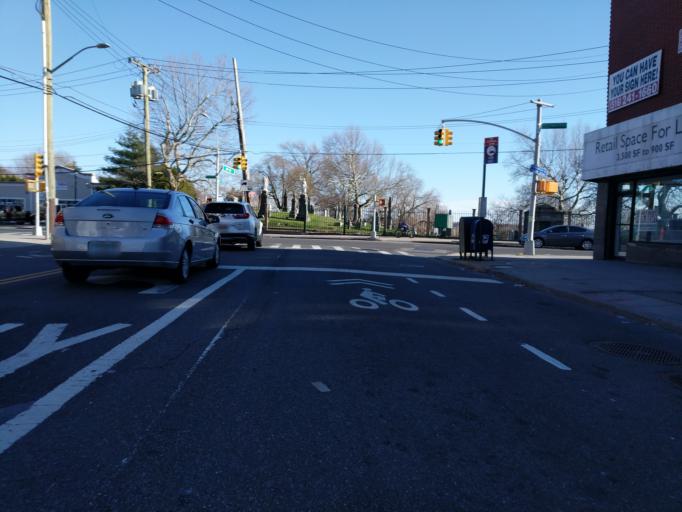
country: US
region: New York
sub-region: Kings County
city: East New York
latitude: 40.7125
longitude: -73.8865
